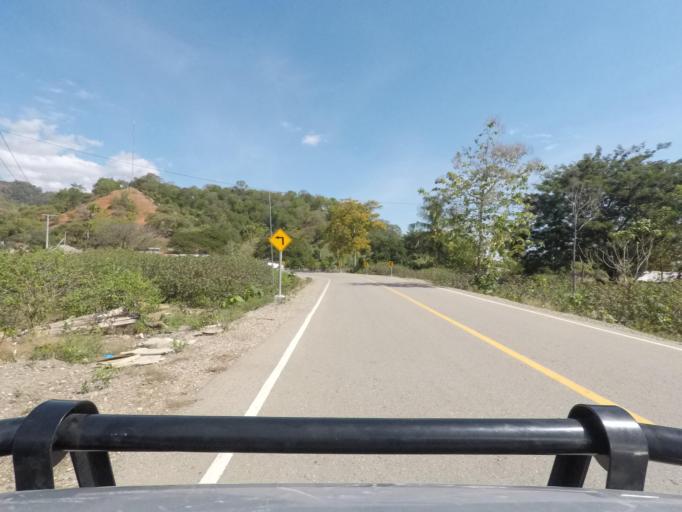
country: TL
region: Bobonaro
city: Maliana
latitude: -8.8699
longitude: 125.0410
